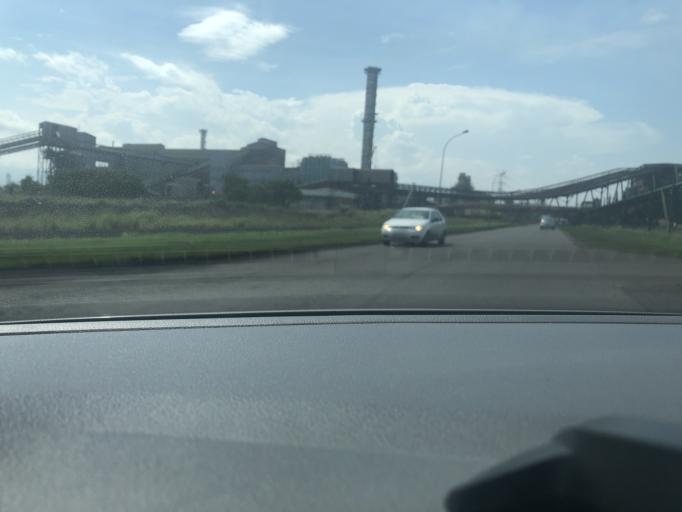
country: BR
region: Rio de Janeiro
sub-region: Itaguai
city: Itaguai
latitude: -22.9155
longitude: -43.7414
